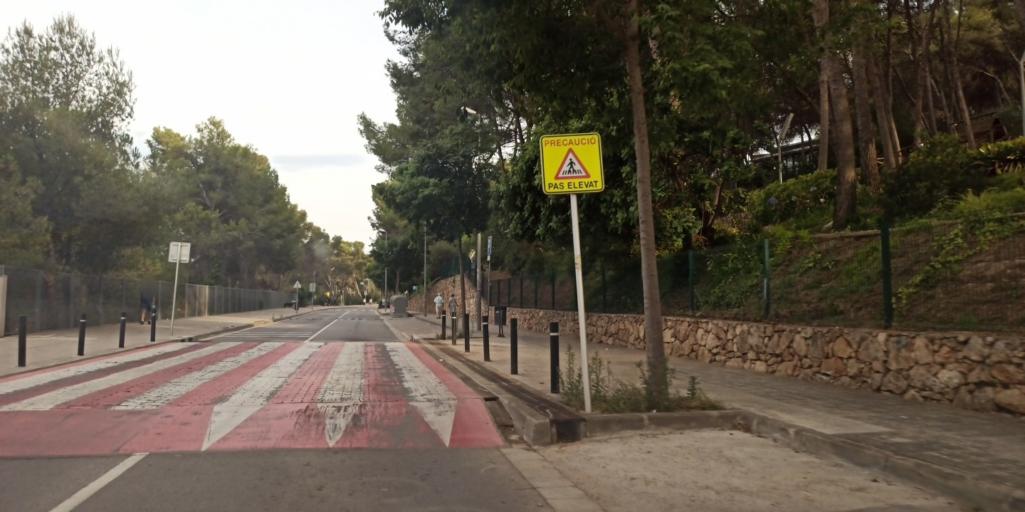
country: ES
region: Catalonia
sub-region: Provincia de Barcelona
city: Castelldefels
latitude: 41.2874
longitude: 1.9731
